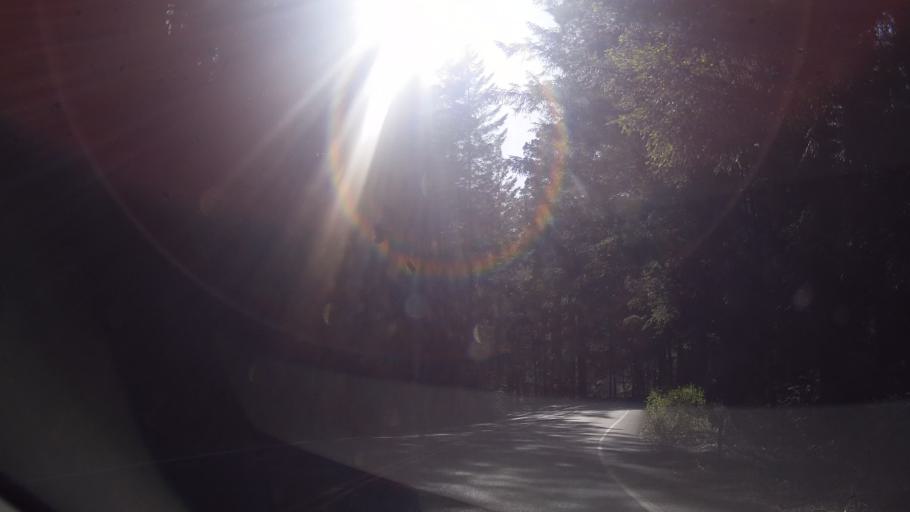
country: US
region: California
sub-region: Mendocino County
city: Brooktrails
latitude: 39.3659
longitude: -123.4994
